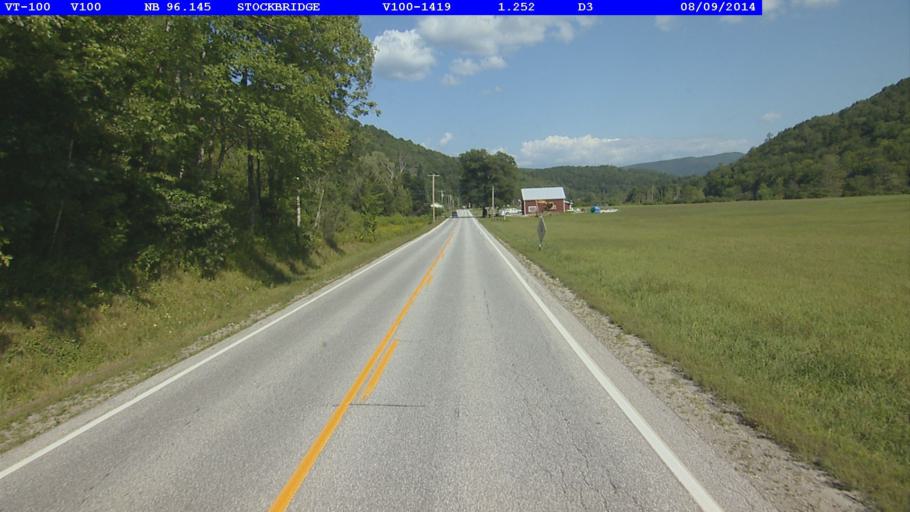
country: US
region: Vermont
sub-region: Orange County
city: Randolph
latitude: 43.7768
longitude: -72.7748
